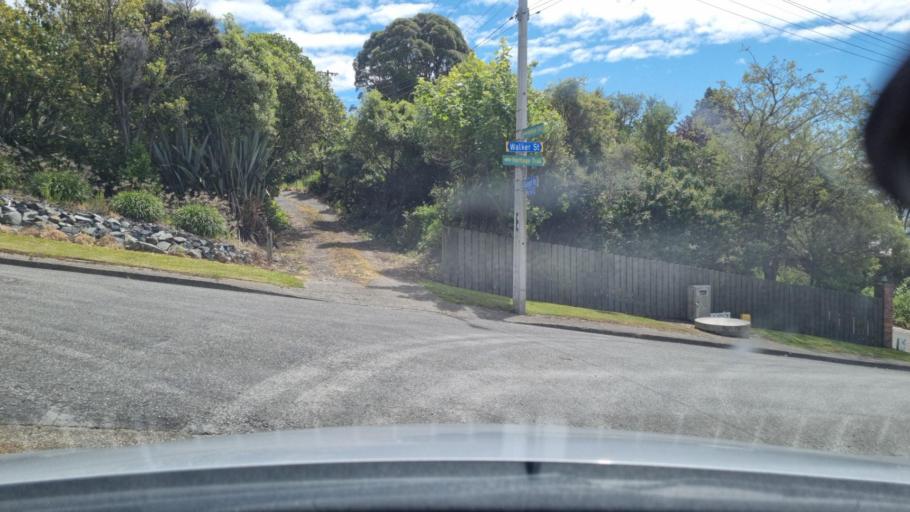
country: NZ
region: Southland
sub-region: Invercargill City
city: Bluff
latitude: -46.6070
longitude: 168.3506
